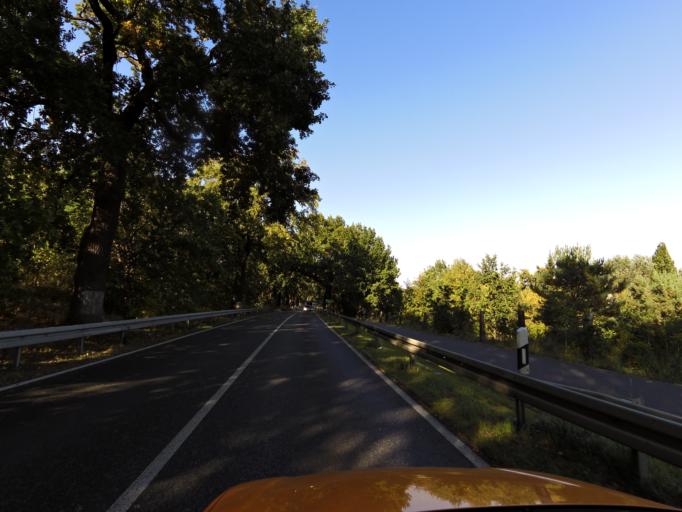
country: DE
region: Brandenburg
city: Potsdam
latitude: 52.4538
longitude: 13.0469
